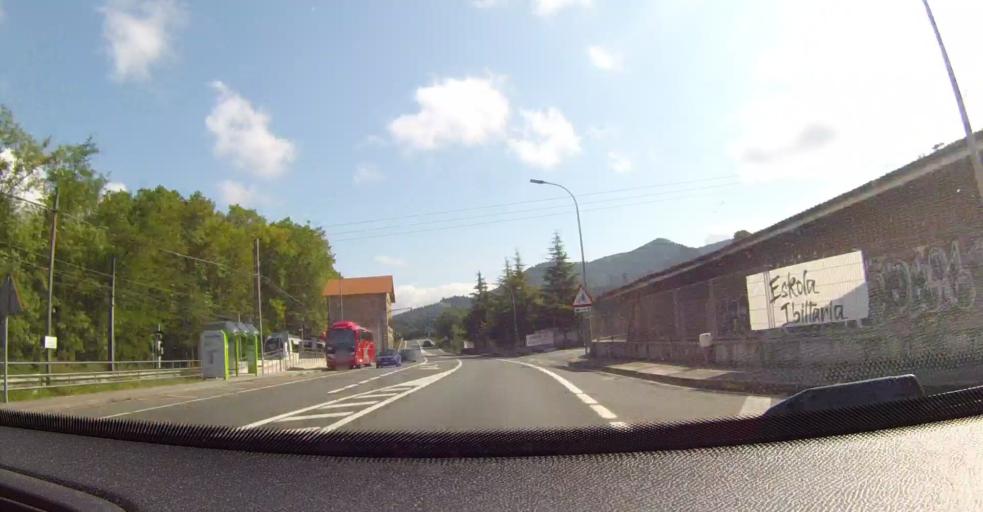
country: ES
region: Basque Country
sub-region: Bizkaia
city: Muxika
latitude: 43.2875
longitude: -2.6895
